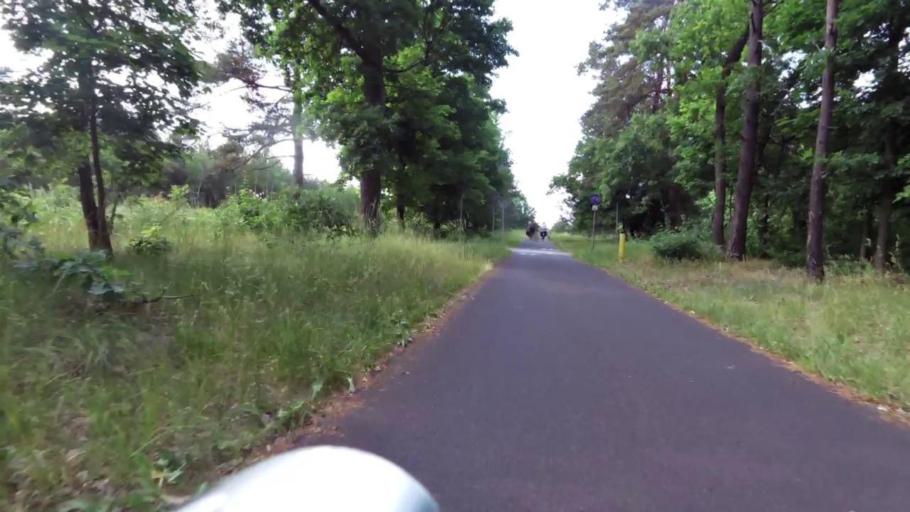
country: PL
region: Kujawsko-Pomorskie
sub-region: Powiat torunski
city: Lysomice
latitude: 53.0755
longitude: 18.5429
